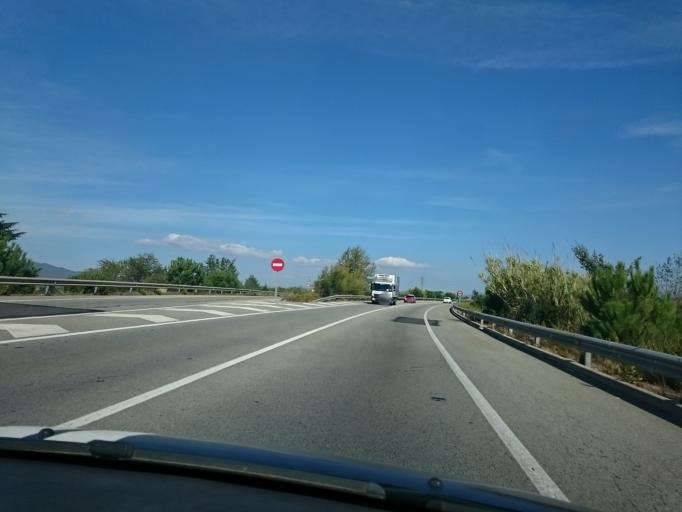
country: ES
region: Catalonia
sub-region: Provincia de Barcelona
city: Santa Perpetua de Mogoda
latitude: 41.5578
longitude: 2.1853
